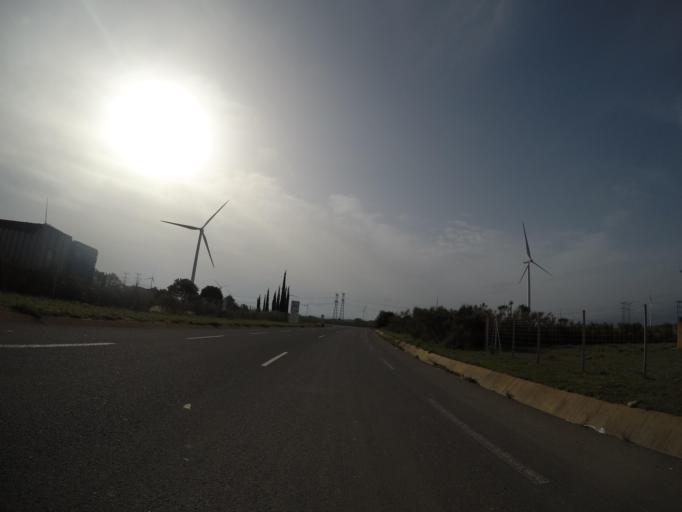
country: FR
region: Languedoc-Roussillon
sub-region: Departement des Pyrenees-Orientales
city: Pezilla-la-Riviere
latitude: 42.7298
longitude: 2.7760
